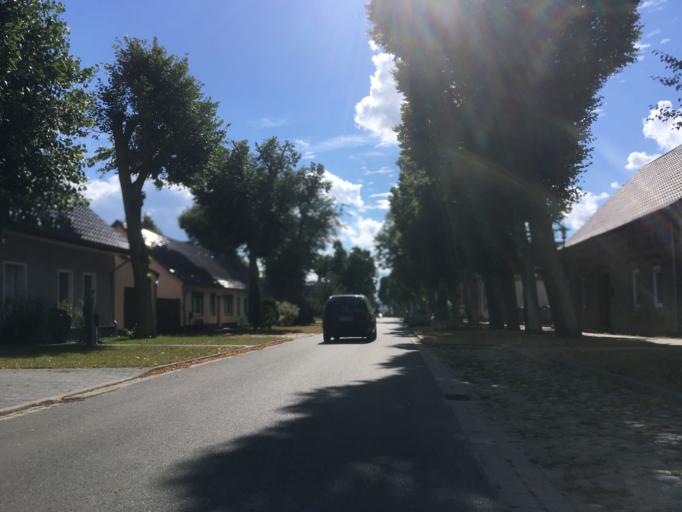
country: DE
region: Brandenburg
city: Angermunde
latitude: 52.9779
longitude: 13.9897
